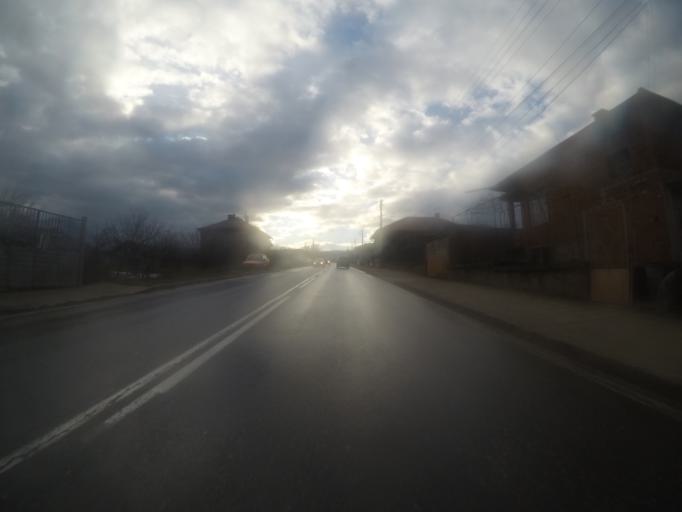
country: BG
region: Blagoevgrad
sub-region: Obshtina Simitli
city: Simitli
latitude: 41.8865
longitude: 23.1190
